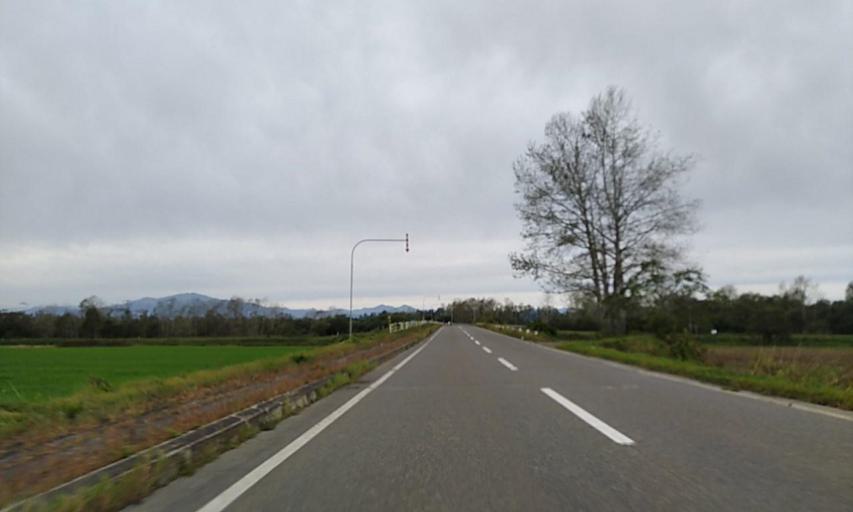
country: JP
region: Hokkaido
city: Obihiro
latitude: 42.7197
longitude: 143.1458
